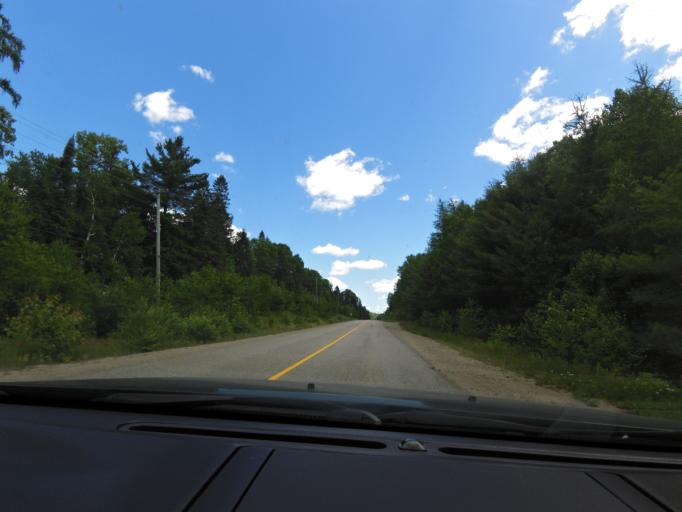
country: CA
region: Ontario
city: Huntsville
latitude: 45.5985
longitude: -79.1928
